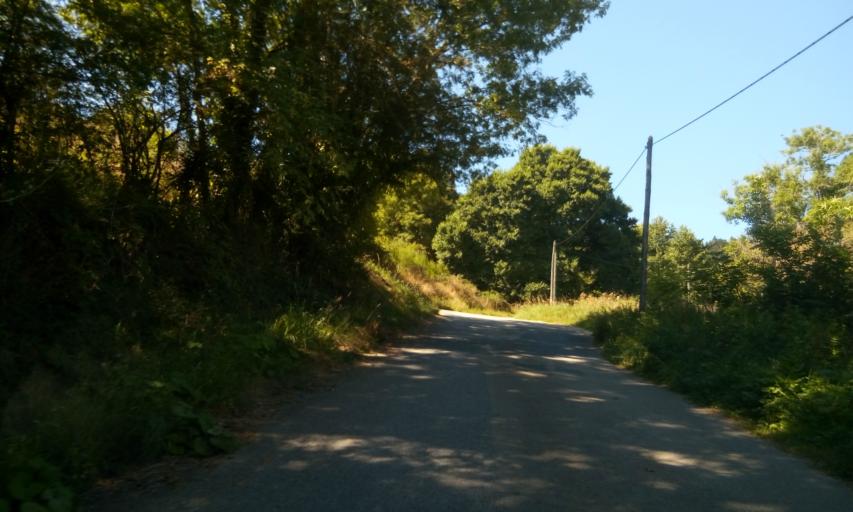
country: FR
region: Rhone-Alpes
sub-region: Departement du Rhone
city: Grandris
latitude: 46.0100
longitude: 4.4430
